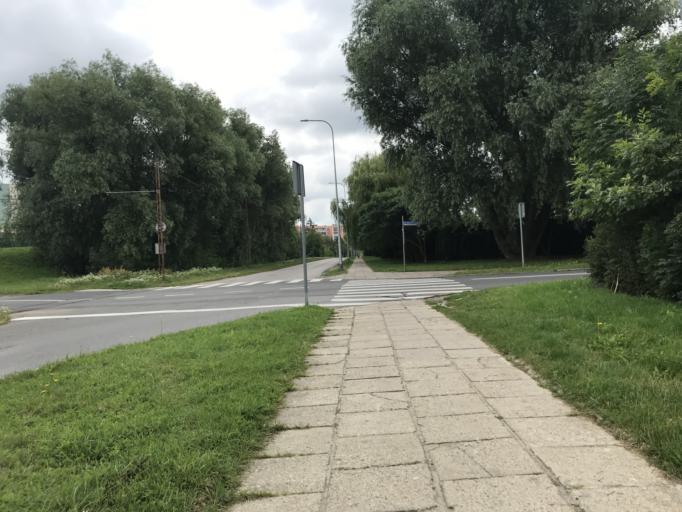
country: PL
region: Warmian-Masurian Voivodeship
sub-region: Powiat elblaski
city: Elblag
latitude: 54.1776
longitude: 19.4262
